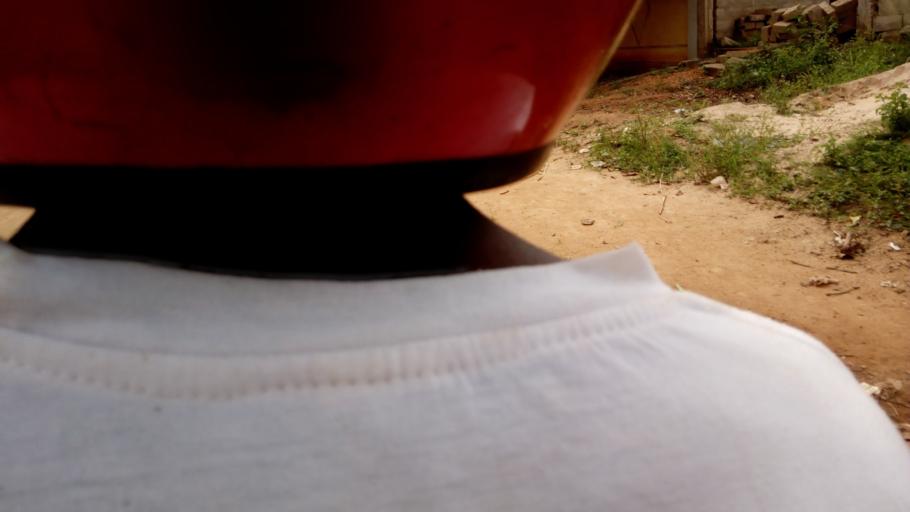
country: TG
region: Maritime
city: Lome
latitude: 6.2219
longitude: 1.1595
